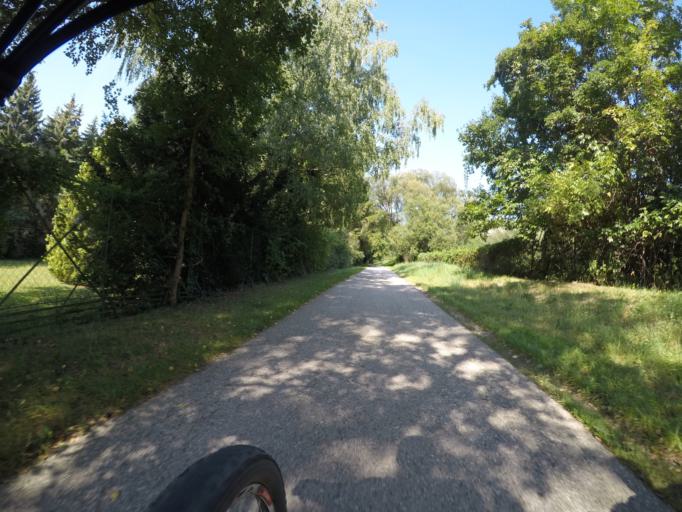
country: AT
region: Lower Austria
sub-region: Politischer Bezirk Baden
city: Berndorf
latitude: 47.9376
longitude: 16.1414
